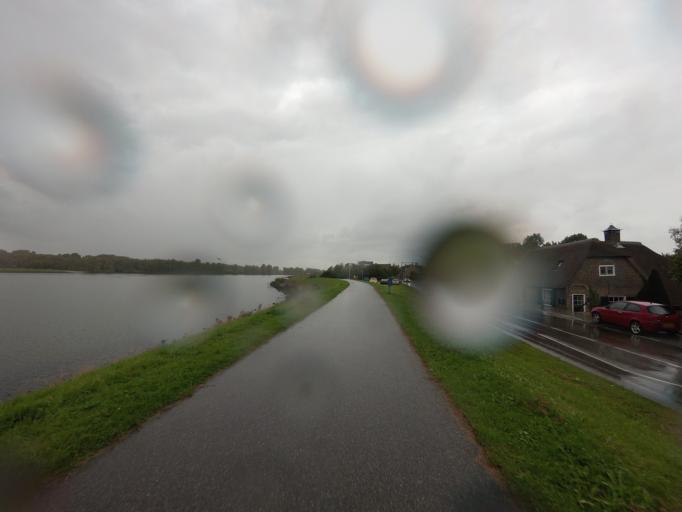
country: NL
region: South Holland
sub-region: Gemeente Alblasserdam
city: Alblasserdam
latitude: 51.8693
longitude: 4.6412
